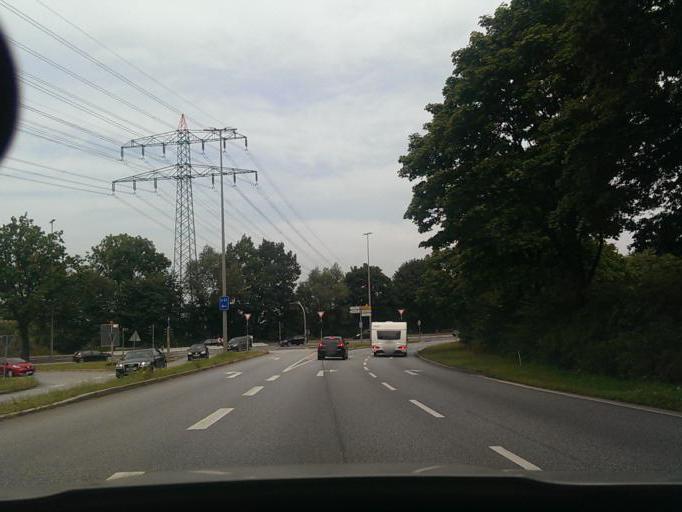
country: DE
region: Schleswig-Holstein
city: Bonningstedt
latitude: 53.6450
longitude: 9.9314
